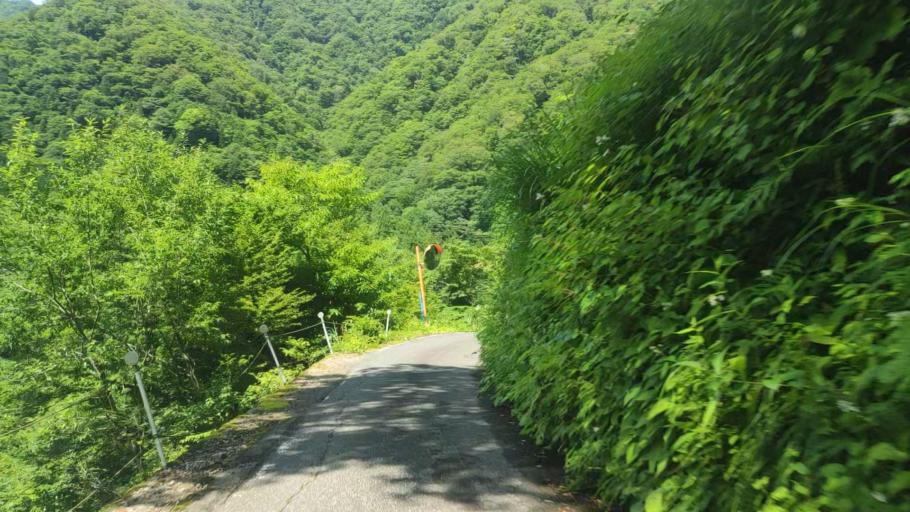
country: JP
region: Fukui
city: Ono
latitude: 35.7675
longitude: 136.5463
